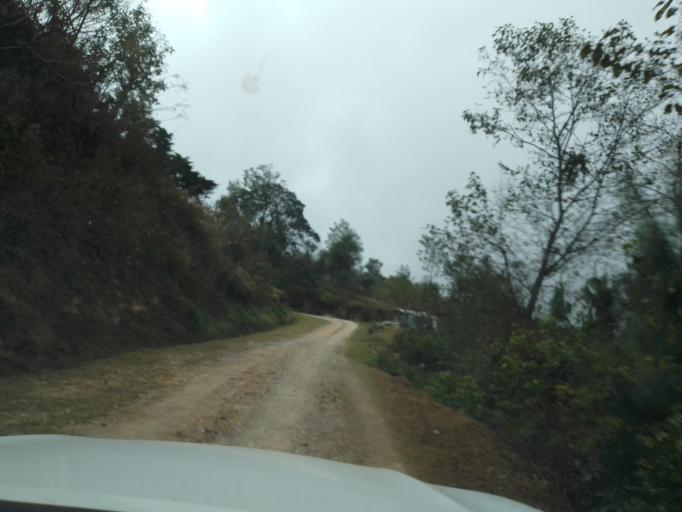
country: MX
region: Chiapas
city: Motozintla de Mendoza
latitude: 15.2197
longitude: -92.2177
